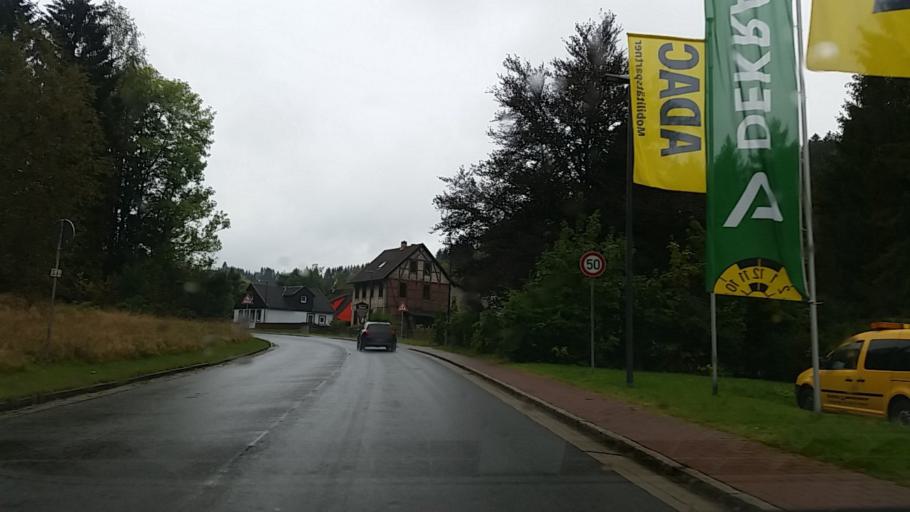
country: DE
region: Lower Saxony
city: Altenau
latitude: 51.8092
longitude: 10.4373
